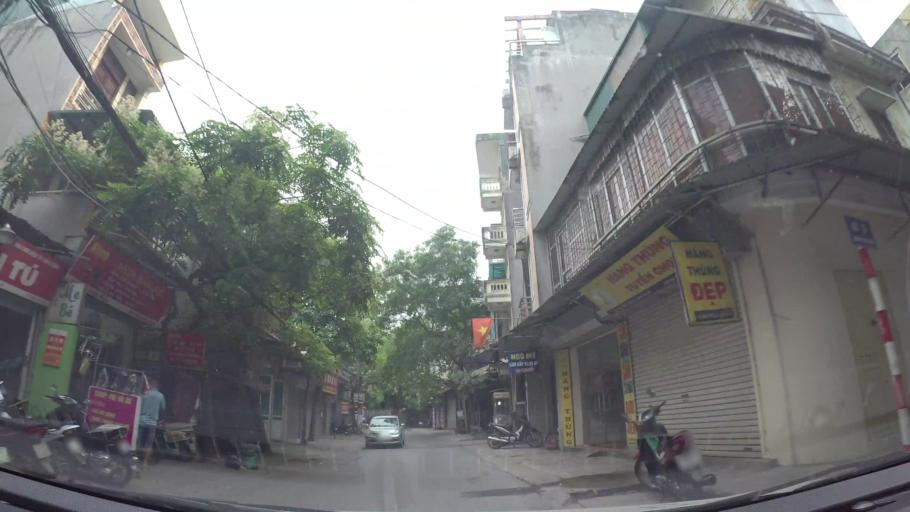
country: VN
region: Ha Noi
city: Cau Dien
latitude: 21.0389
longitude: 105.7584
